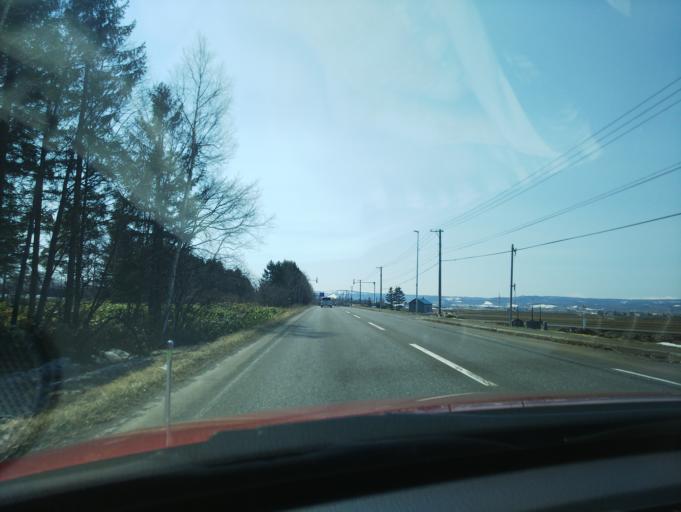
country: JP
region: Hokkaido
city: Nayoro
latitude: 44.3087
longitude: 142.4439
